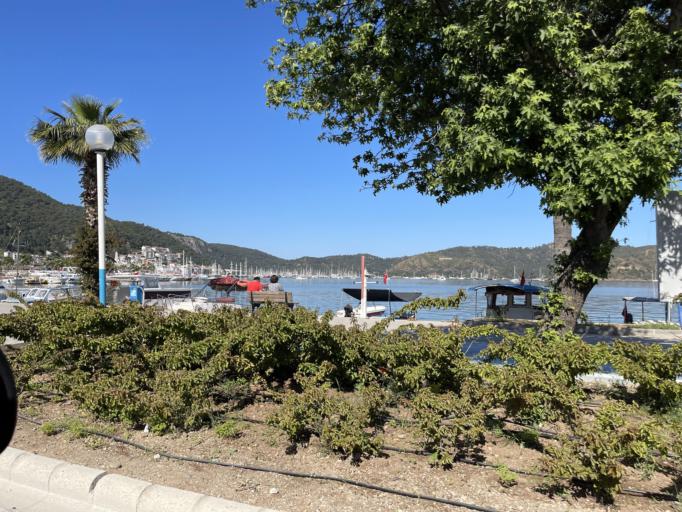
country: TR
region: Mugla
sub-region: Fethiye
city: Fethiye
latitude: 36.6263
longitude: 29.1163
